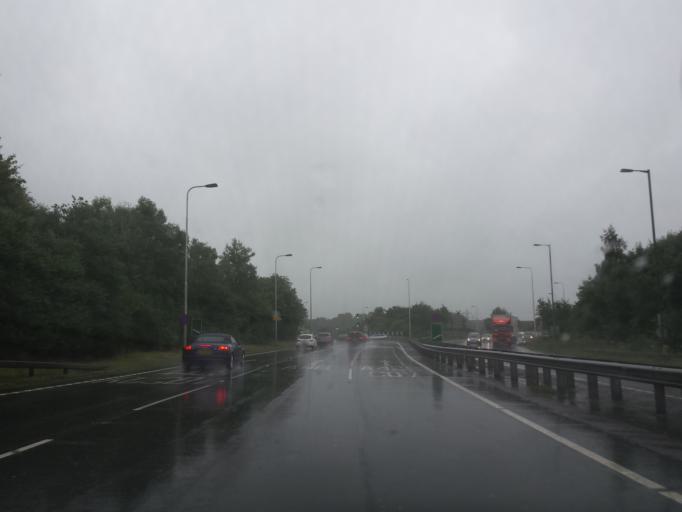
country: GB
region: England
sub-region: Warwickshire
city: Ryton on Dunsmore
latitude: 52.3972
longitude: -1.4309
